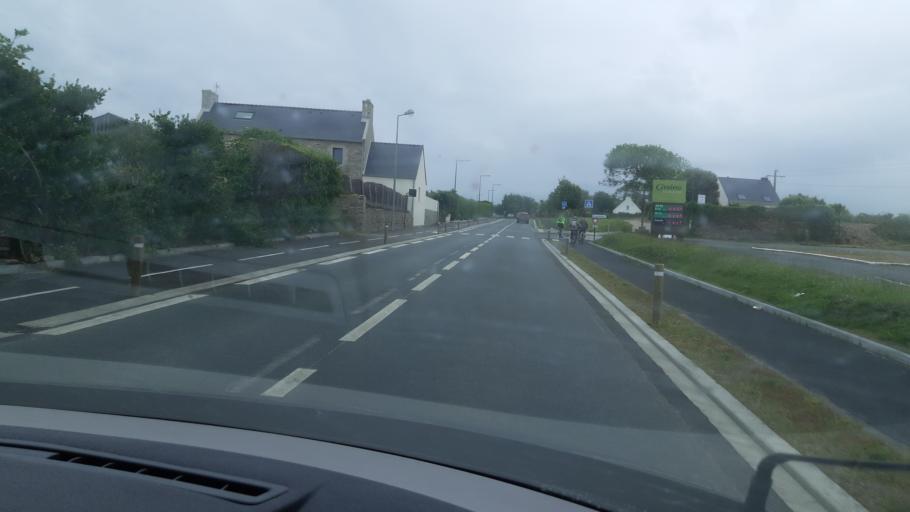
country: FR
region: Brittany
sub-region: Departement du Finistere
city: Roscoff
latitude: 48.7140
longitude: -3.9846
